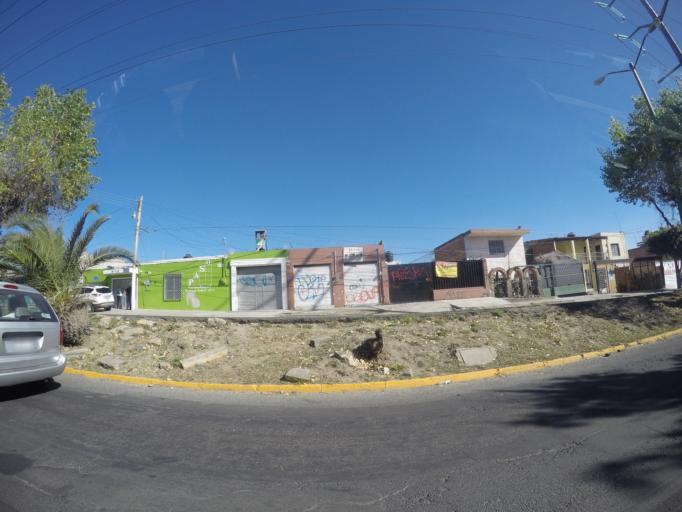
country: MX
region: Jalisco
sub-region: Zapopan
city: Zapopan
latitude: 20.7260
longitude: -103.3453
